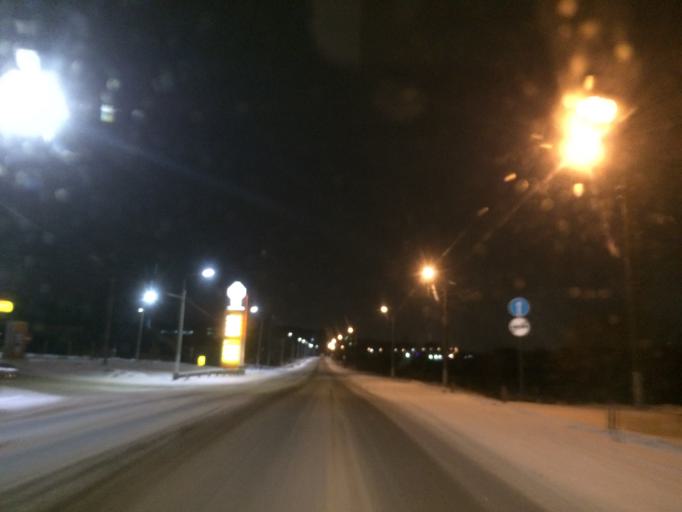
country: RU
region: Tula
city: Tula
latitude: 54.2290
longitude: 37.6549
